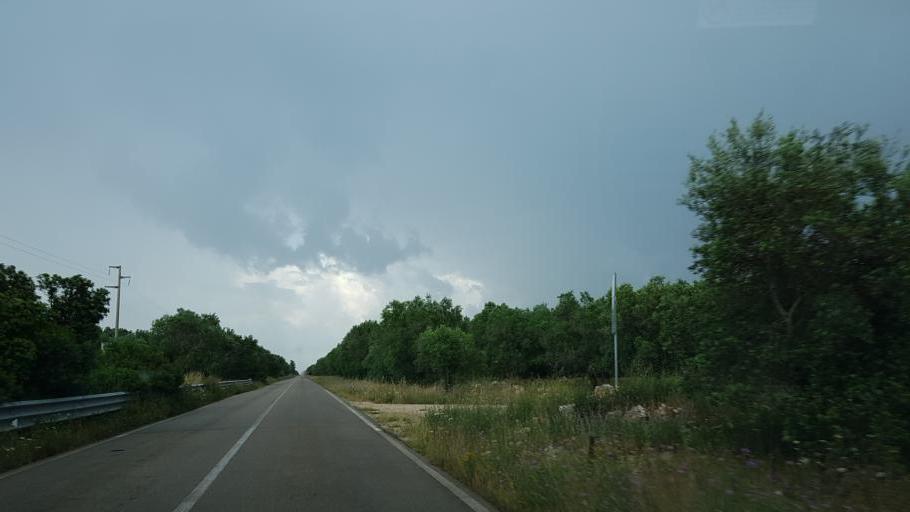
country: IT
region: Apulia
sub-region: Provincia di Brindisi
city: San Pancrazio Salentino
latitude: 40.3475
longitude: 17.8468
